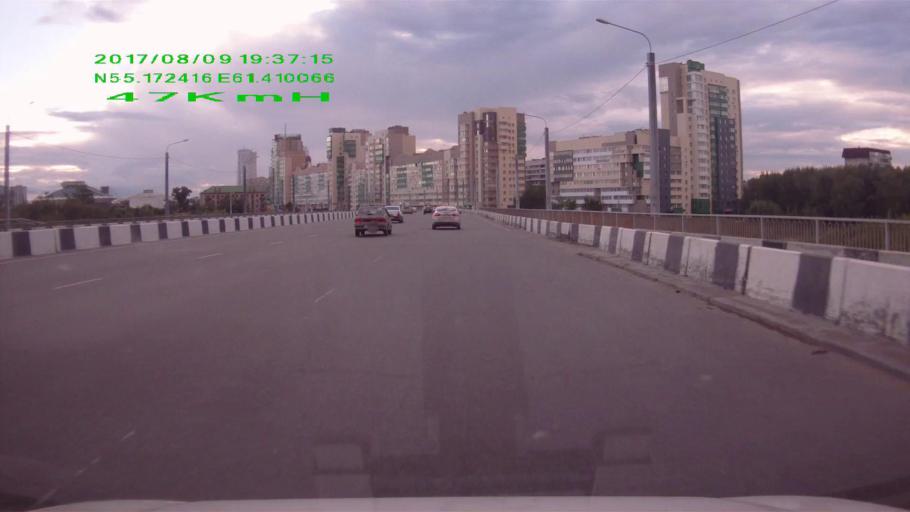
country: RU
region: Chelyabinsk
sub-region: Gorod Chelyabinsk
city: Chelyabinsk
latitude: 55.1725
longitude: 61.4087
